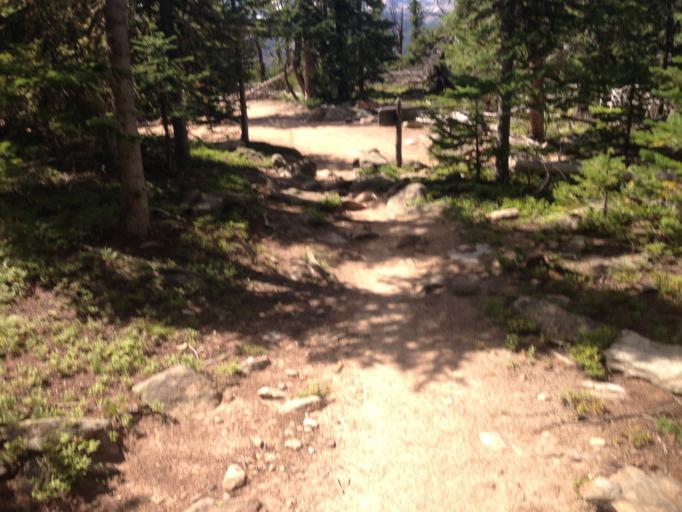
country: US
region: Colorado
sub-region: Larimer County
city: Estes Park
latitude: 40.1995
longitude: -105.5702
